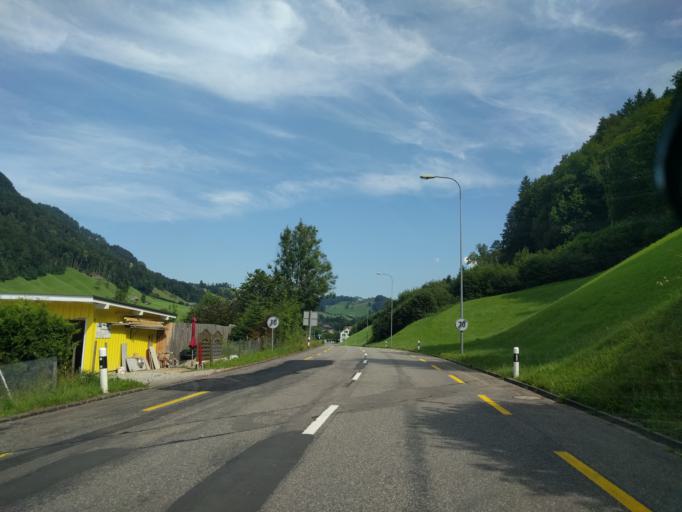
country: CH
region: Saint Gallen
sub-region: Wahlkreis Toggenburg
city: Mogelsberg
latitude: 47.3283
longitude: 9.1394
